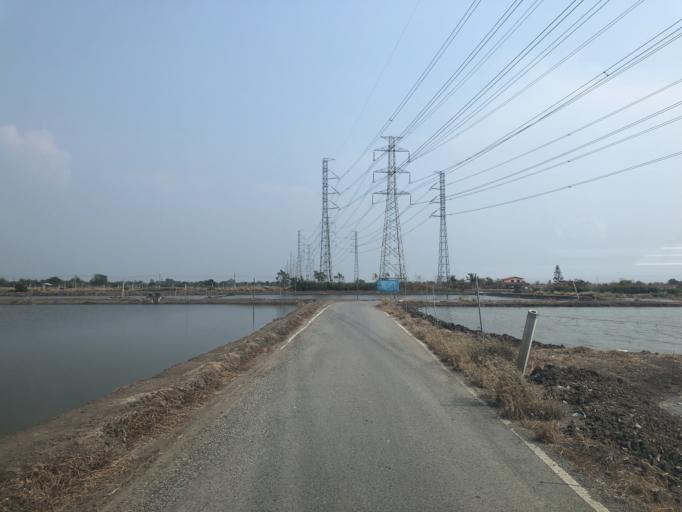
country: TH
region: Samut Prakan
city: Bang Bo
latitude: 13.5431
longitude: 100.8866
